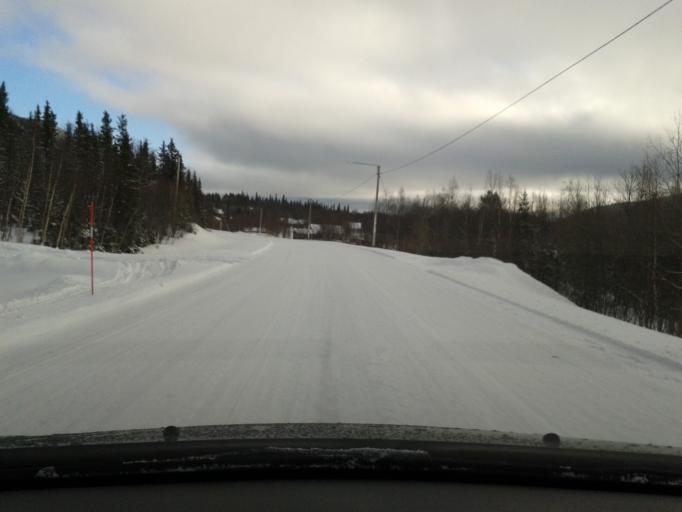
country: SE
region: Vaesterbotten
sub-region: Vilhelmina Kommun
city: Sjoberg
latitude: 65.2520
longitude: 15.5455
